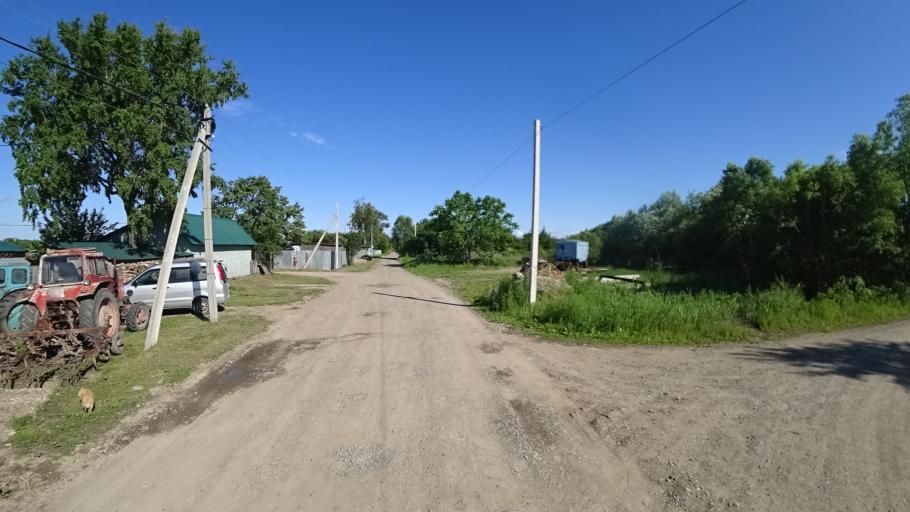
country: RU
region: Khabarovsk Krai
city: Khor
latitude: 47.8854
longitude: 135.0178
